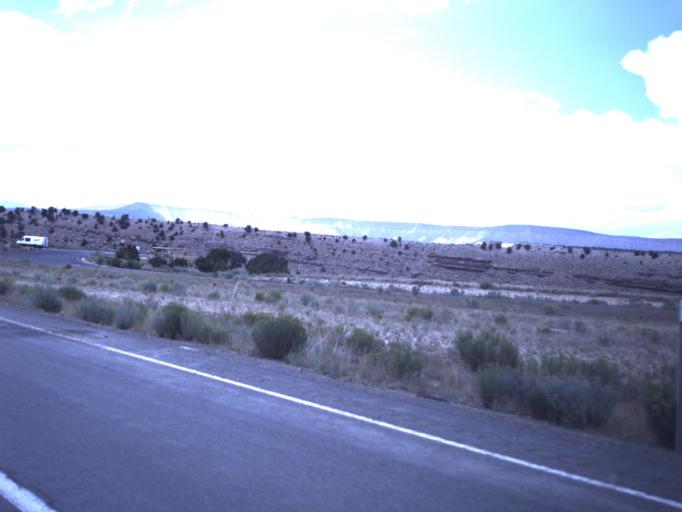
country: US
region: Utah
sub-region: Duchesne County
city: Duchesne
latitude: 40.1725
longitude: -110.4905
